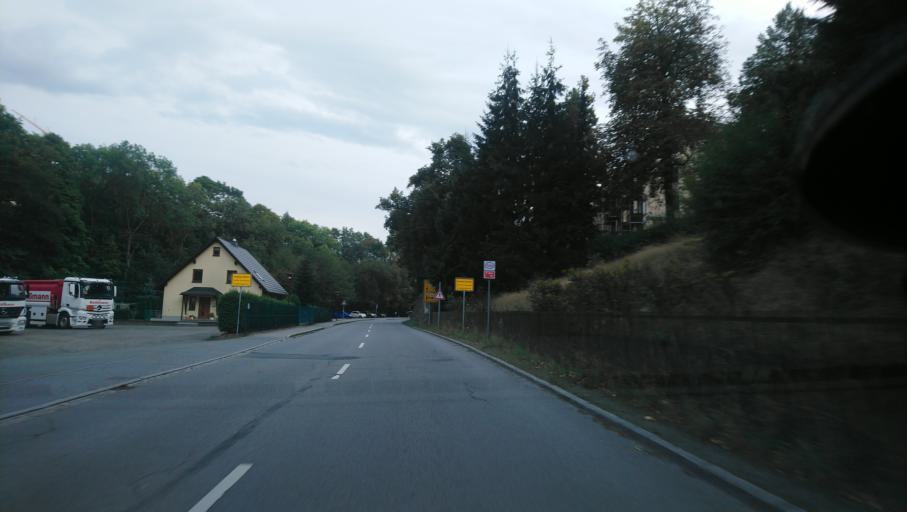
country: DE
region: Saxony
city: Annaberg-Buchholz
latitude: 50.5789
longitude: 12.9968
